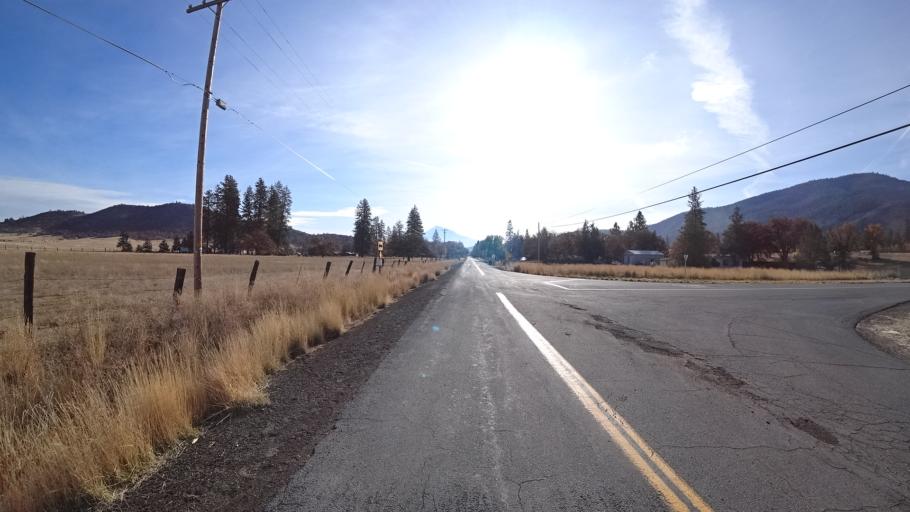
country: US
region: California
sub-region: Siskiyou County
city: Yreka
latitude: 41.6693
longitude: -122.6094
